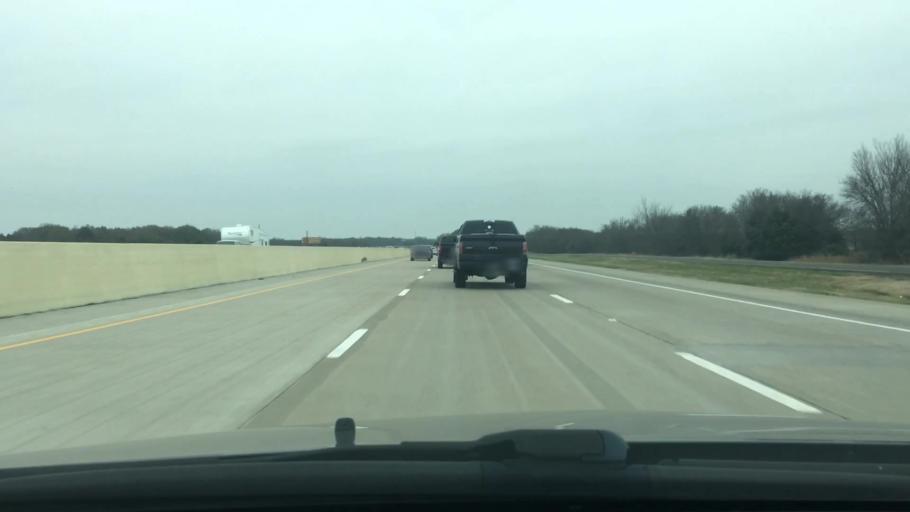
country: US
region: Texas
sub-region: Navarro County
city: Corsicana
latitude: 31.9731
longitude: -96.4227
